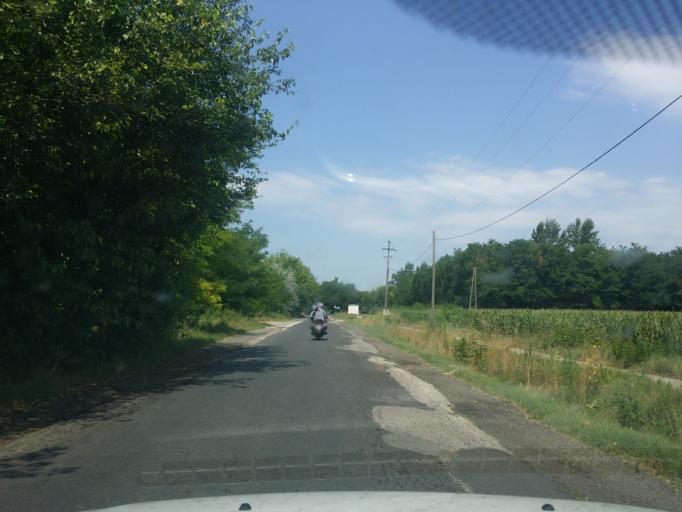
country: HU
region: Bacs-Kiskun
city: Jaszszentlaszlo
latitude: 46.5835
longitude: 19.7269
